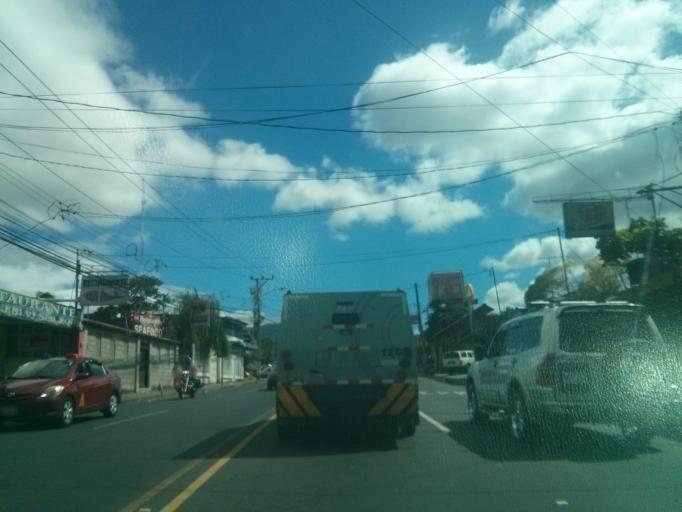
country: CR
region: San Jose
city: San Juan de Dios
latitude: 9.8928
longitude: -84.0820
